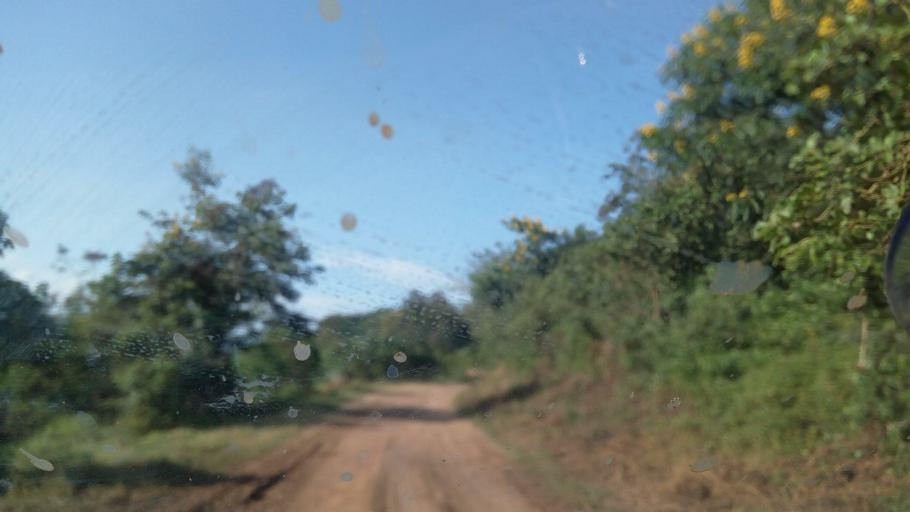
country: BI
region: Bururi
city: Rumonge
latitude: -4.2760
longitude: 28.9714
